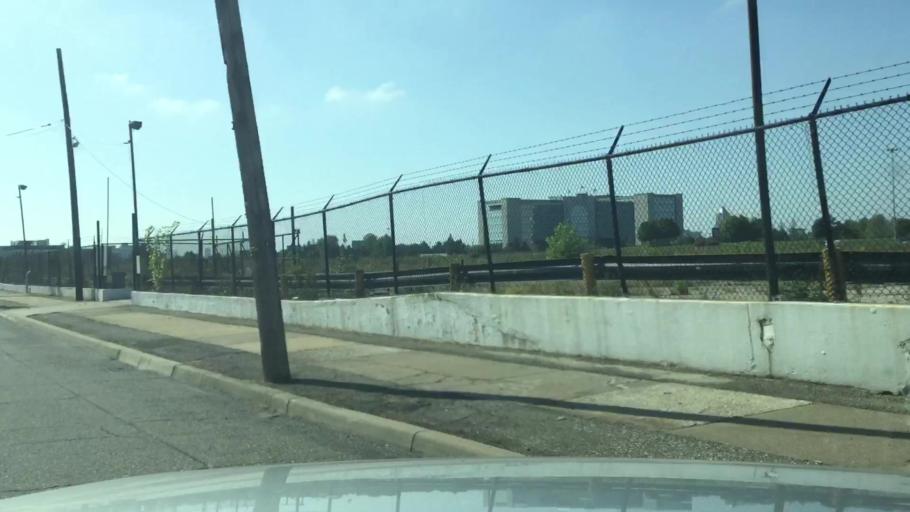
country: US
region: Michigan
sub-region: Wayne County
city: Hamtramck
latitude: 42.3926
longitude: -83.0661
